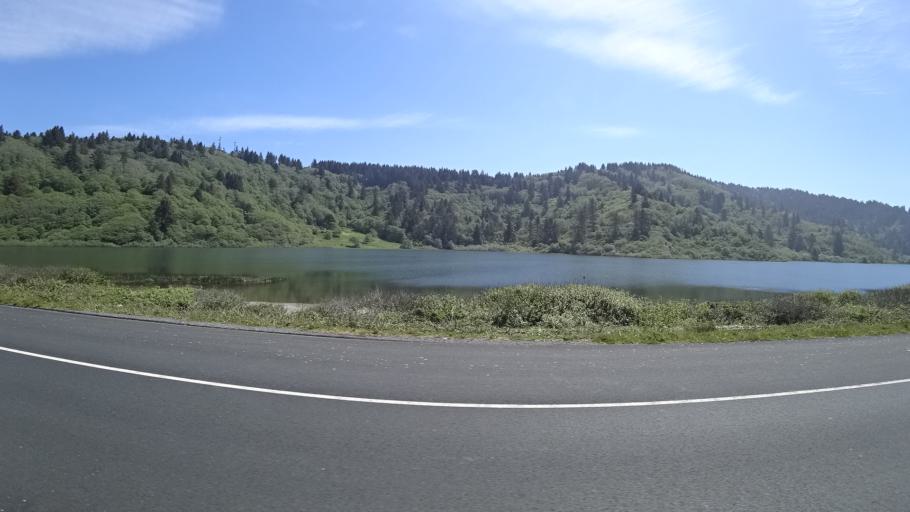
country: US
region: California
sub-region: Humboldt County
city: Westhaven-Moonstone
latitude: 41.2750
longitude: -124.0948
